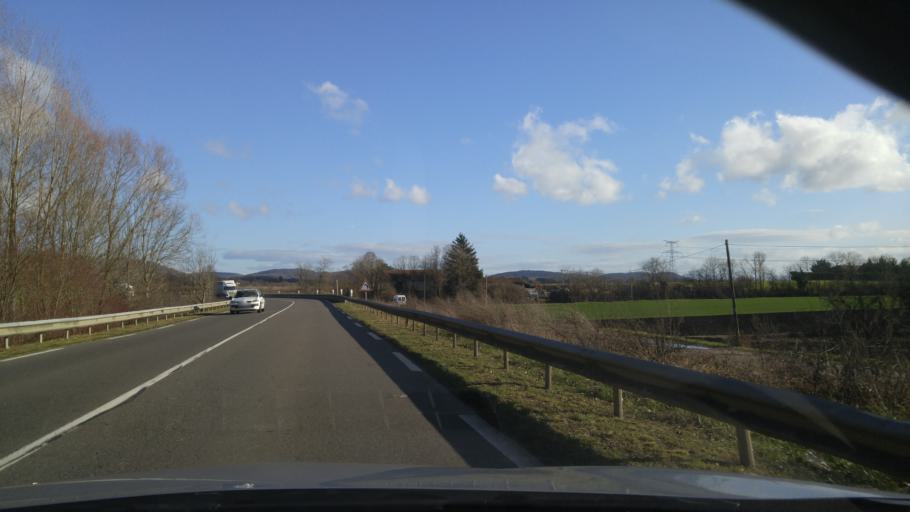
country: FR
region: Rhone-Alpes
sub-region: Departement de l'Isere
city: Chamagnieu
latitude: 45.6703
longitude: 5.1480
